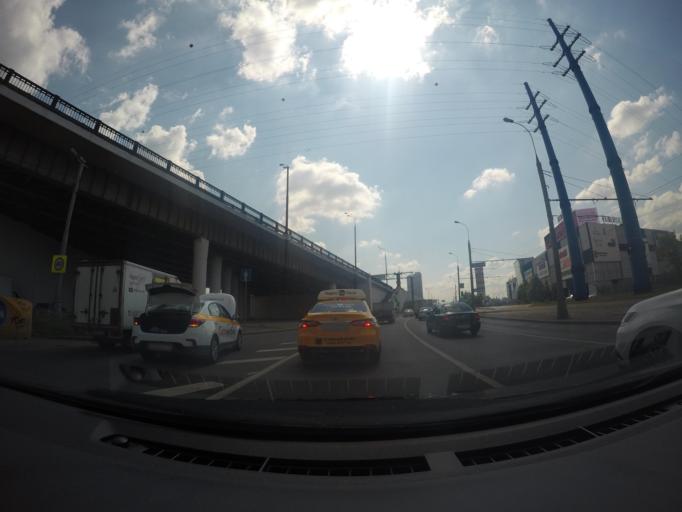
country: RU
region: Moscow
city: Rostokino
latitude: 55.8465
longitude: 37.6702
